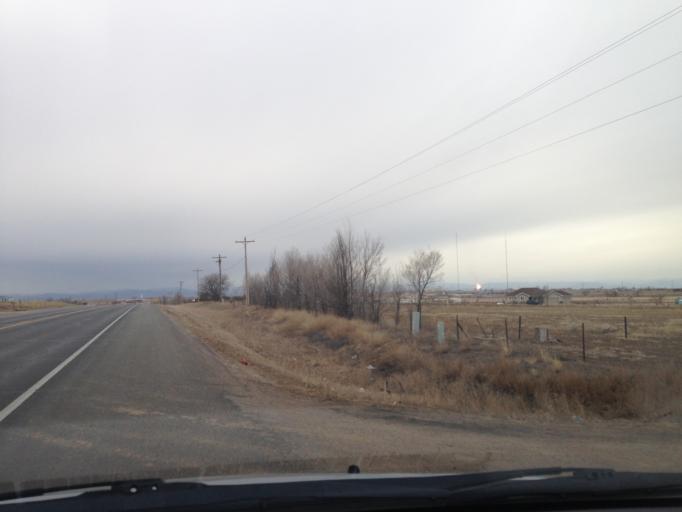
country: US
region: Colorado
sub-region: Weld County
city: Fort Lupton
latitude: 40.0801
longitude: -104.8613
